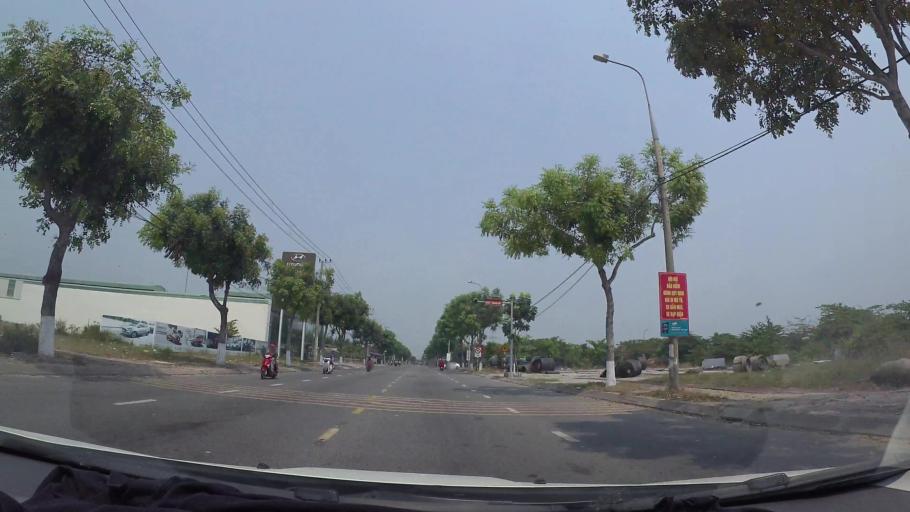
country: VN
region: Da Nang
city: Cam Le
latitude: 15.9936
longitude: 108.2075
